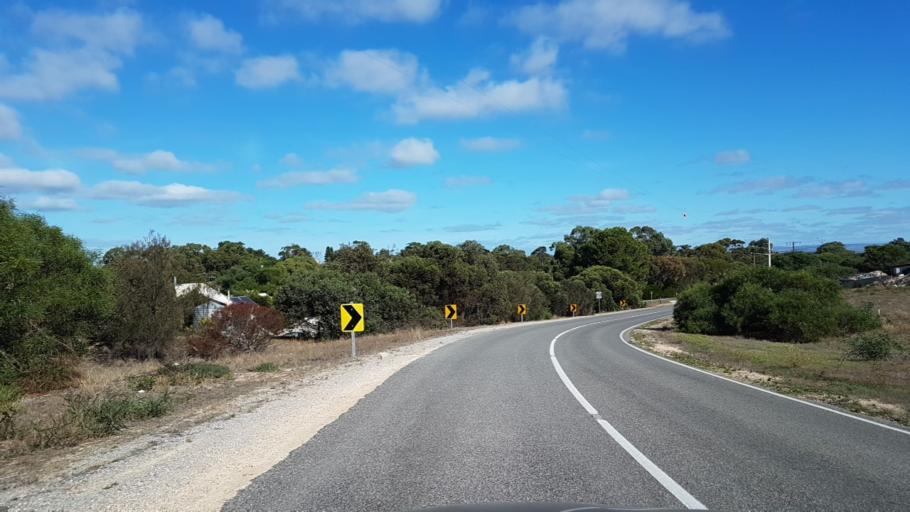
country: AU
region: South Australia
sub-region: Alexandrina
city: Goolwa
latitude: -35.4919
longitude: 138.9302
